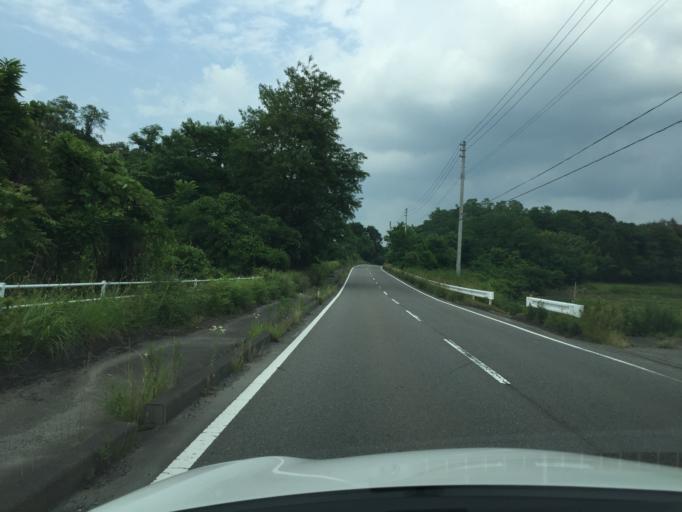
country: JP
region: Fukushima
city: Sukagawa
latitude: 37.3003
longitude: 140.4355
